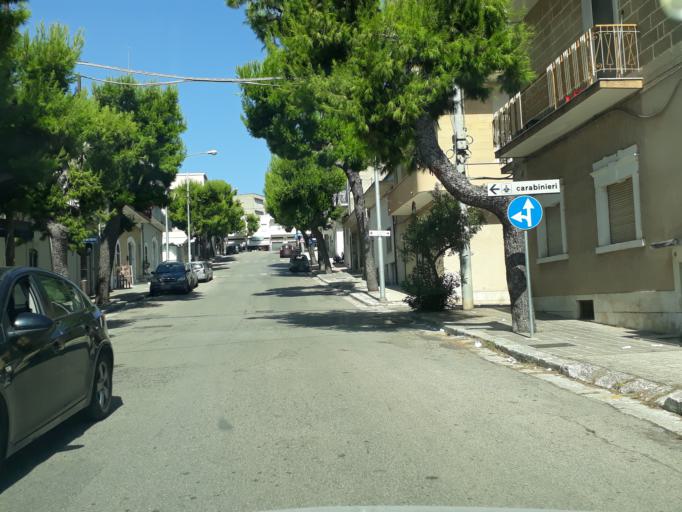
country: IT
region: Apulia
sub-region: Provincia di Brindisi
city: Carovigno
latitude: 40.7048
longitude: 17.6619
